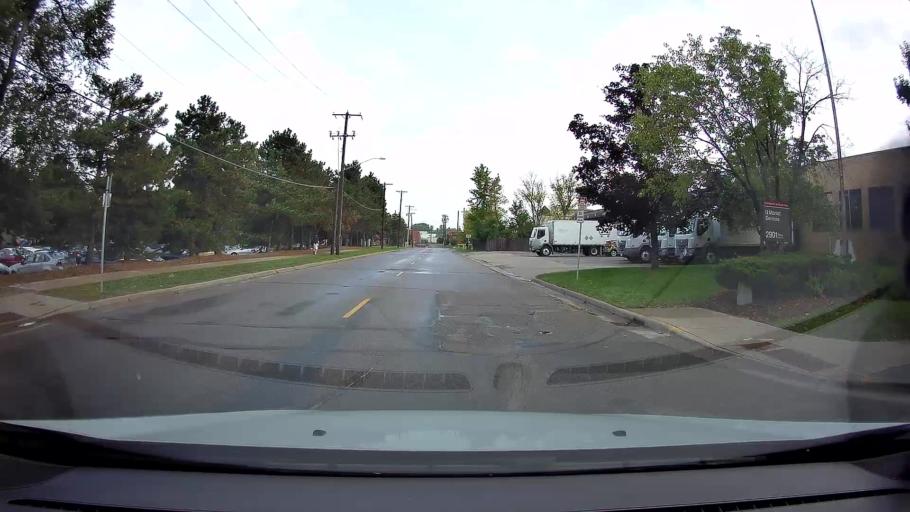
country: US
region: Minnesota
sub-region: Ramsey County
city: Lauderdale
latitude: 44.9899
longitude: -93.2126
